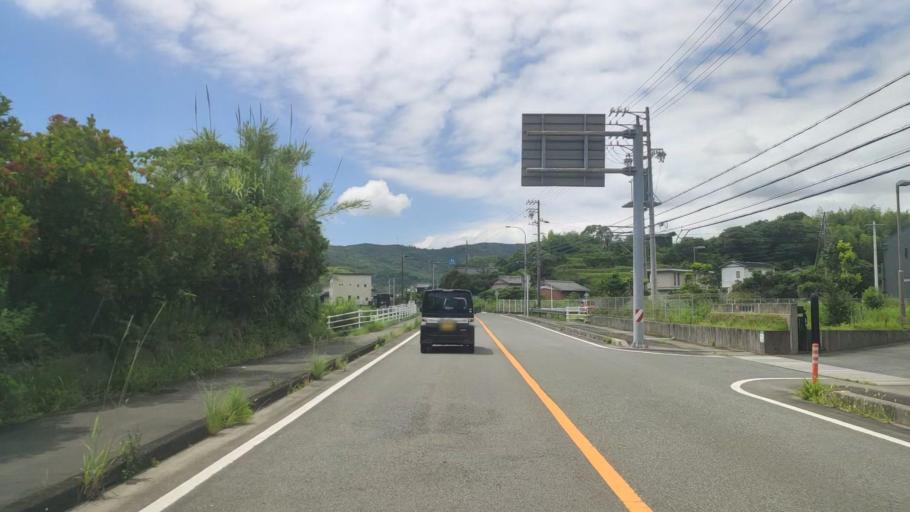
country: JP
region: Mie
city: Toba
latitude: 34.4381
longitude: 136.8415
